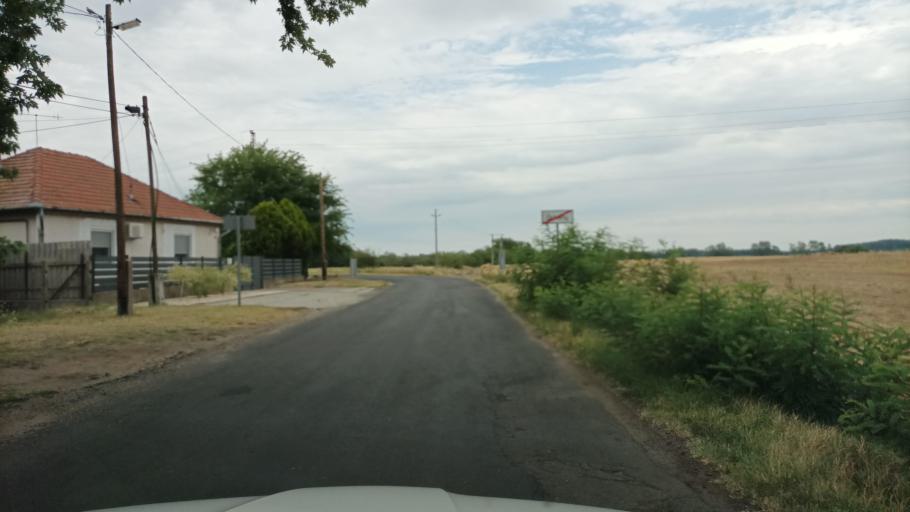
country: HU
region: Pest
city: Orkeny
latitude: 47.1302
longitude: 19.4522
